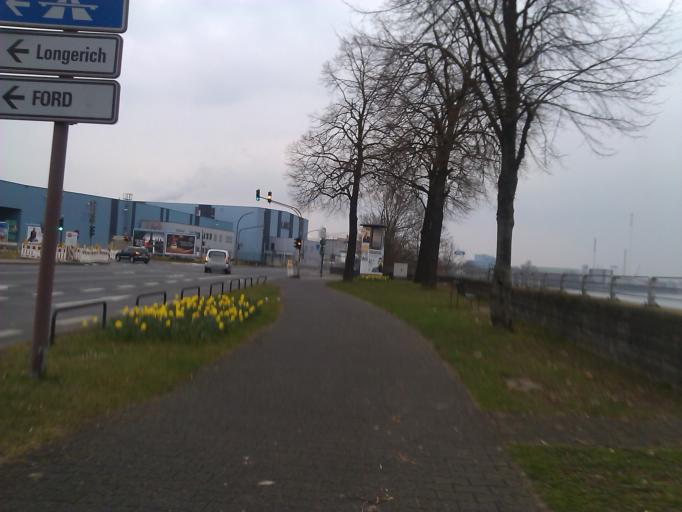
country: DE
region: North Rhine-Westphalia
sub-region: Regierungsbezirk Koln
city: Nippes
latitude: 50.9959
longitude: 6.9605
